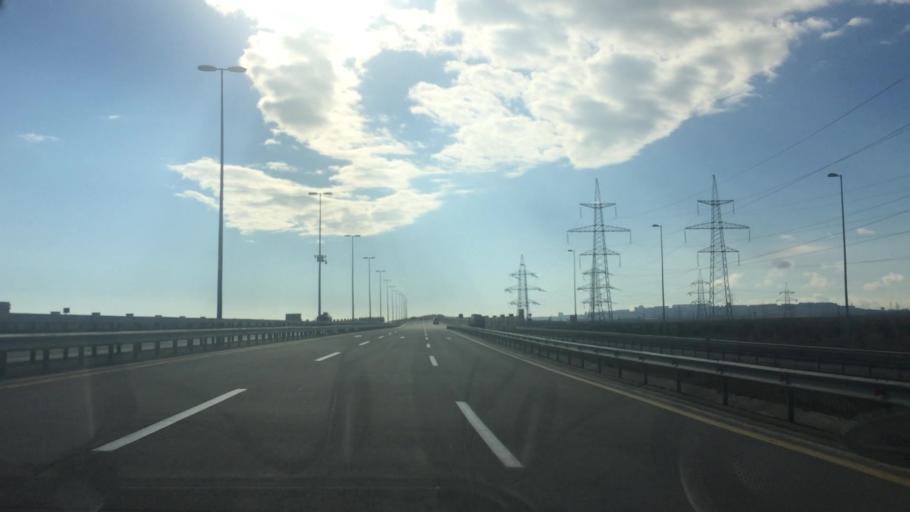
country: AZ
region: Baki
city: Hovsan
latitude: 40.3944
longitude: 50.0794
